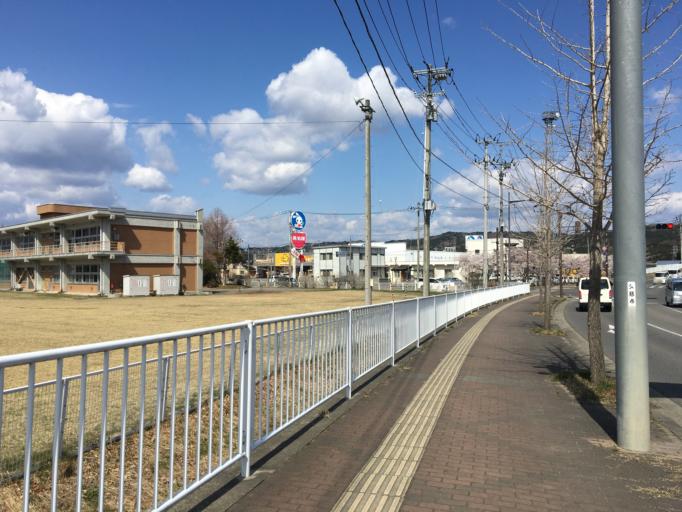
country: JP
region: Aomori
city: Hachinohe
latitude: 40.1910
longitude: 141.7778
